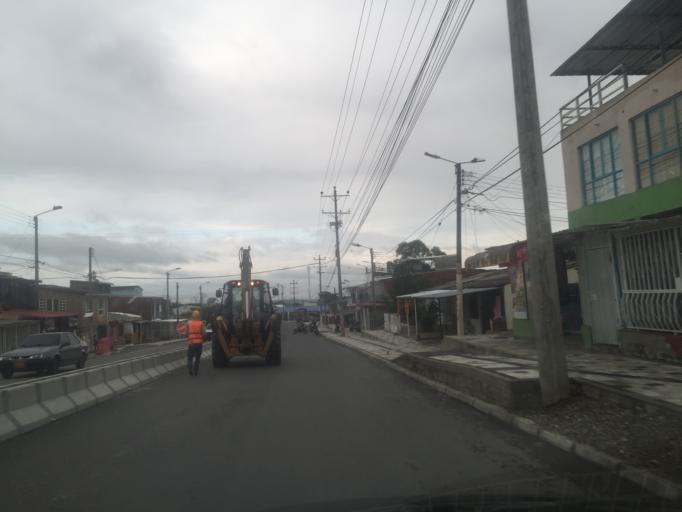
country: CO
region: Quindio
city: Armenia
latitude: 4.5189
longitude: -75.7104
